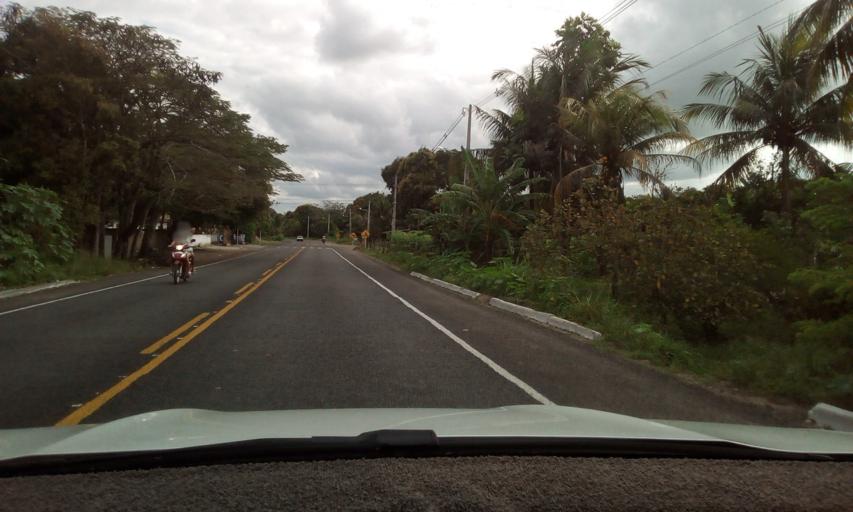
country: BR
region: Paraiba
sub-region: Mamanguape
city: Mamanguape
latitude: -6.8212
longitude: -35.1055
